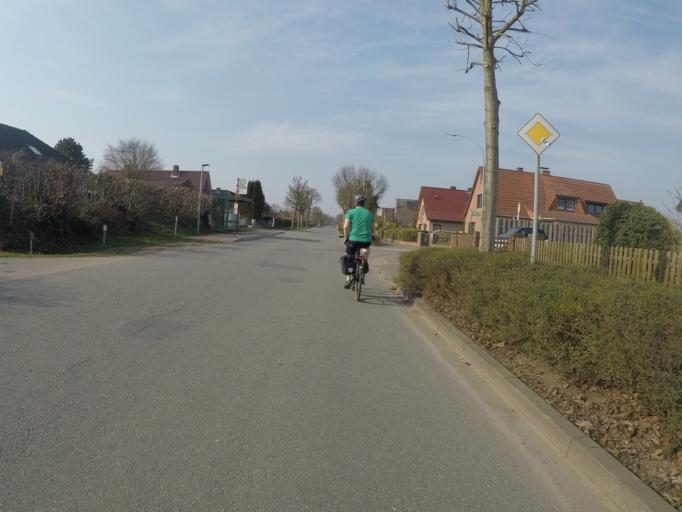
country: DE
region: Schleswig-Holstein
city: Kukels
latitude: 53.9007
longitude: 10.2329
